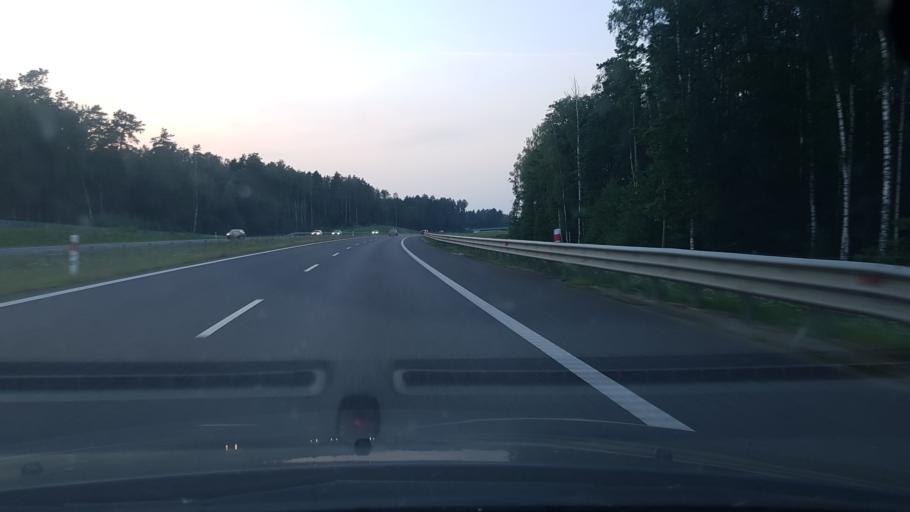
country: PL
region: Warmian-Masurian Voivodeship
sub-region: Powiat olsztynski
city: Olsztynek
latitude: 53.4539
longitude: 20.3223
